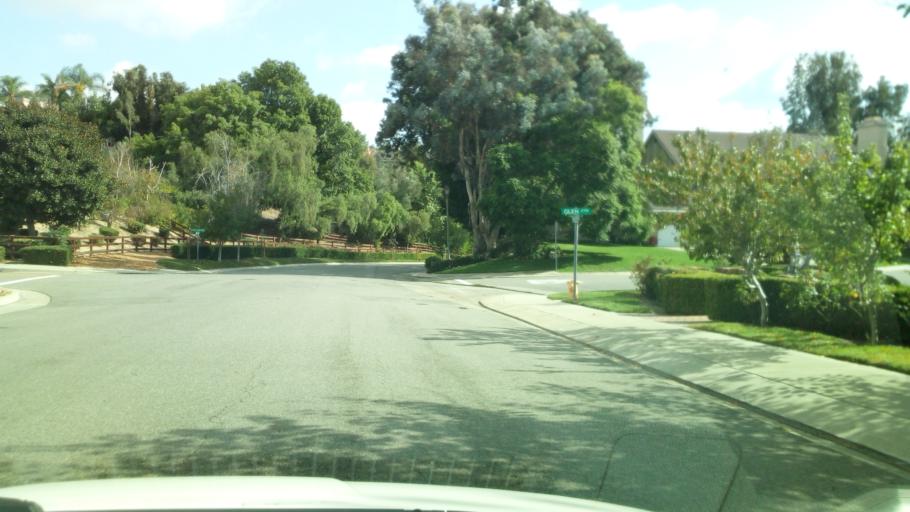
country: US
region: California
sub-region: Orange County
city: Mission Viejo
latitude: 33.5817
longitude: -117.6836
